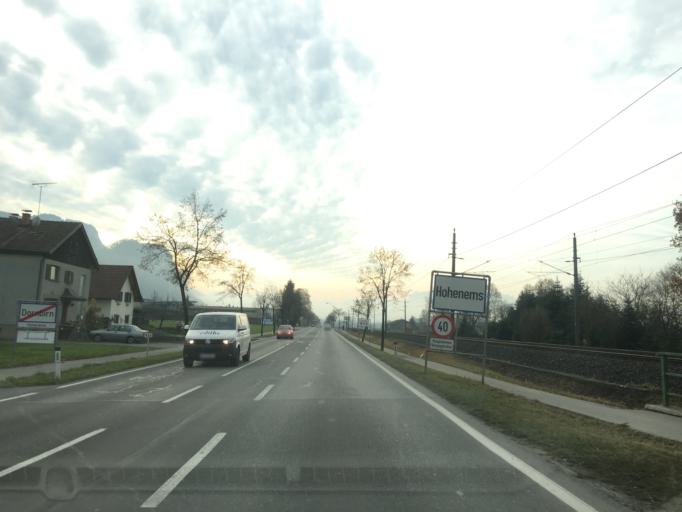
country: AT
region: Vorarlberg
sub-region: Politischer Bezirk Dornbirn
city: Hohenems
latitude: 47.3858
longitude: 9.7130
